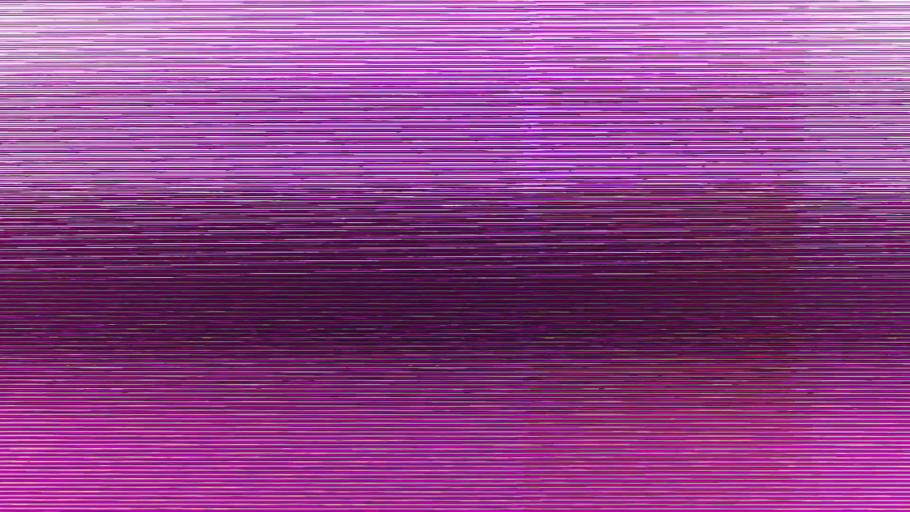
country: US
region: Michigan
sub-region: Washtenaw County
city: Ann Arbor
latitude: 42.3118
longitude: -83.6928
